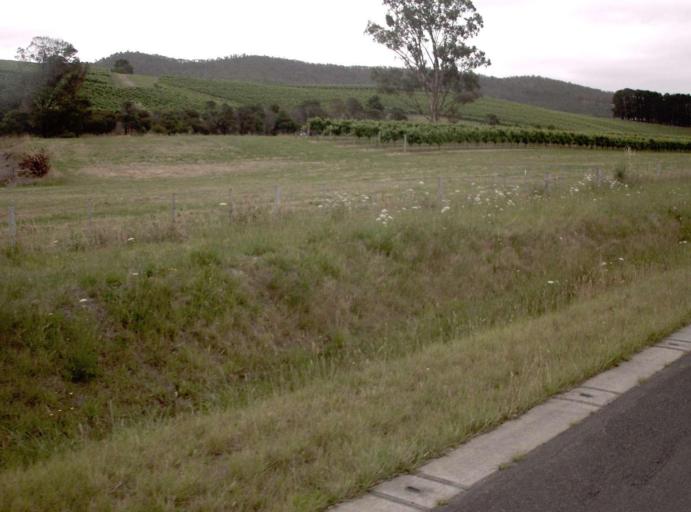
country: AU
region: Victoria
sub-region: Yarra Ranges
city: Yarra Glen
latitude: -37.5974
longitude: 145.4178
